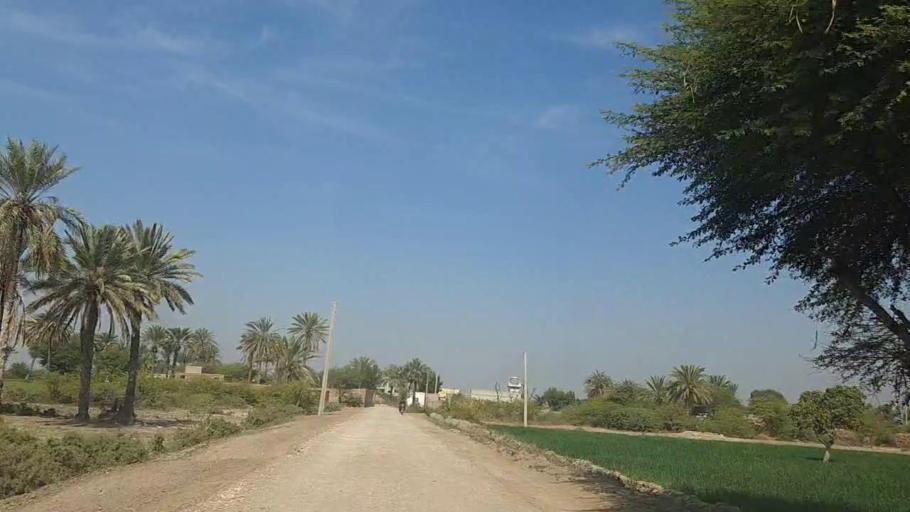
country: PK
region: Sindh
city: Mirpur Khas
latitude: 25.4881
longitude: 68.9651
